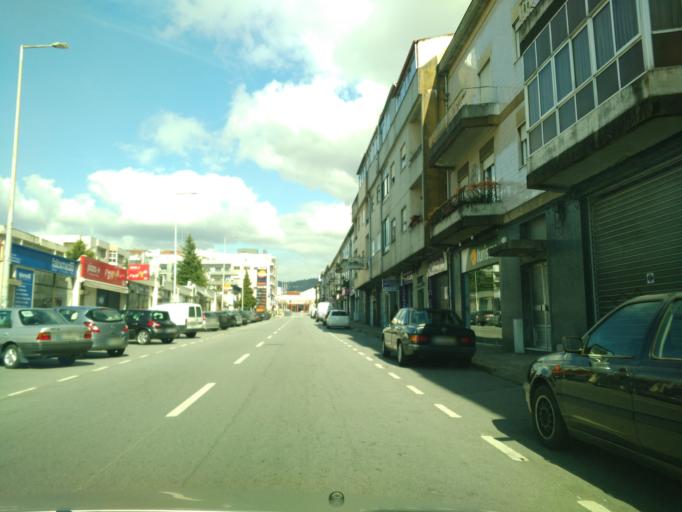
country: PT
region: Braga
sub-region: Braga
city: Braga
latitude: 41.5431
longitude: -8.4216
